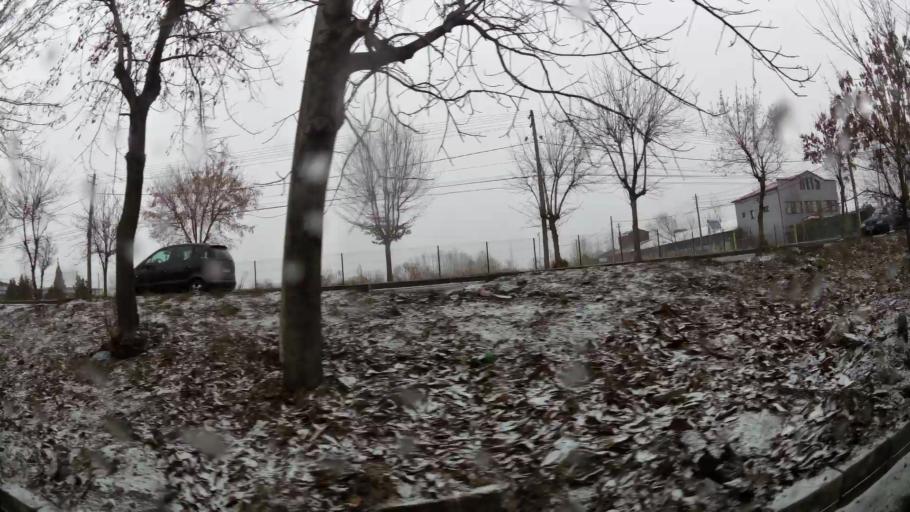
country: RO
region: Dambovita
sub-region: Municipiul Targoviste
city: Targoviste
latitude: 44.9111
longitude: 25.4527
